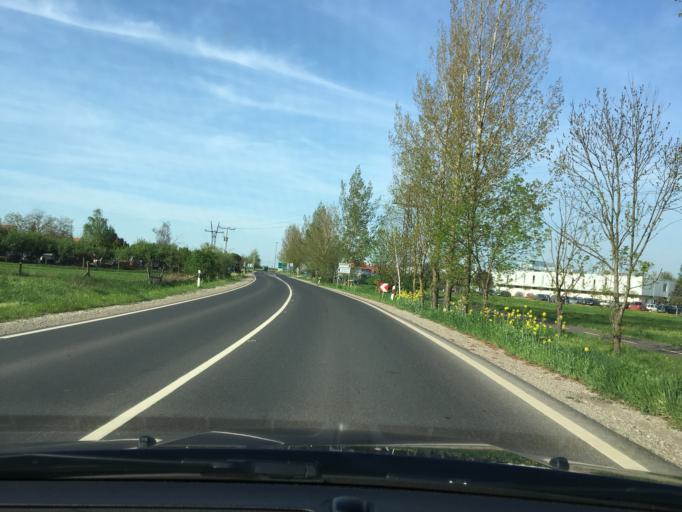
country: HU
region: Bekes
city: Bekescsaba
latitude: 46.6816
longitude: 21.0483
